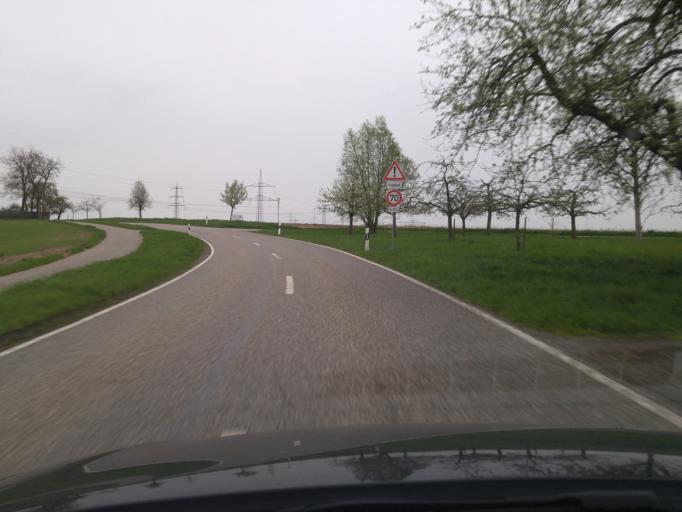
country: DE
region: Baden-Wuerttemberg
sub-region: Regierungsbezirk Stuttgart
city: Bad Rappenau
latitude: 49.2529
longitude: 9.1130
